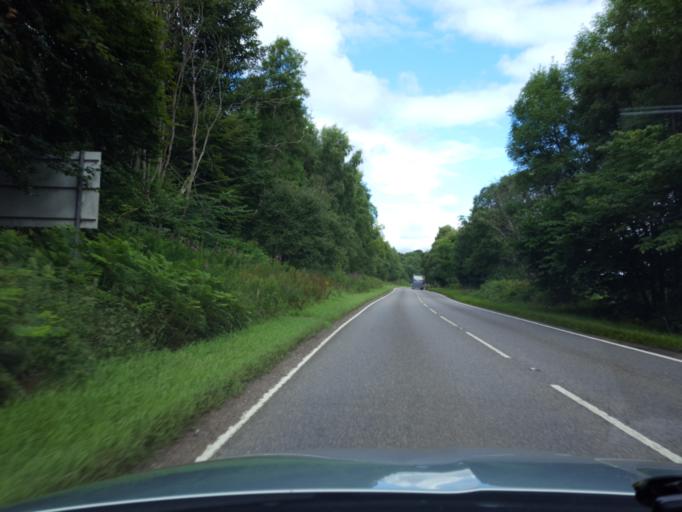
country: GB
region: Scotland
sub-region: Moray
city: Rothes
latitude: 57.5057
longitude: -3.1971
